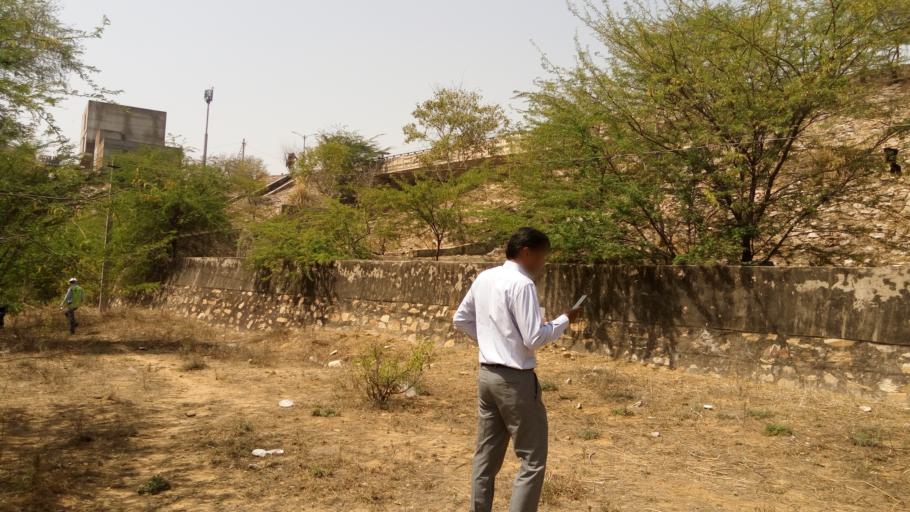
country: IN
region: Rajasthan
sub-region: Jaipur
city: Jaipur
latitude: 26.9398
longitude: 75.7828
